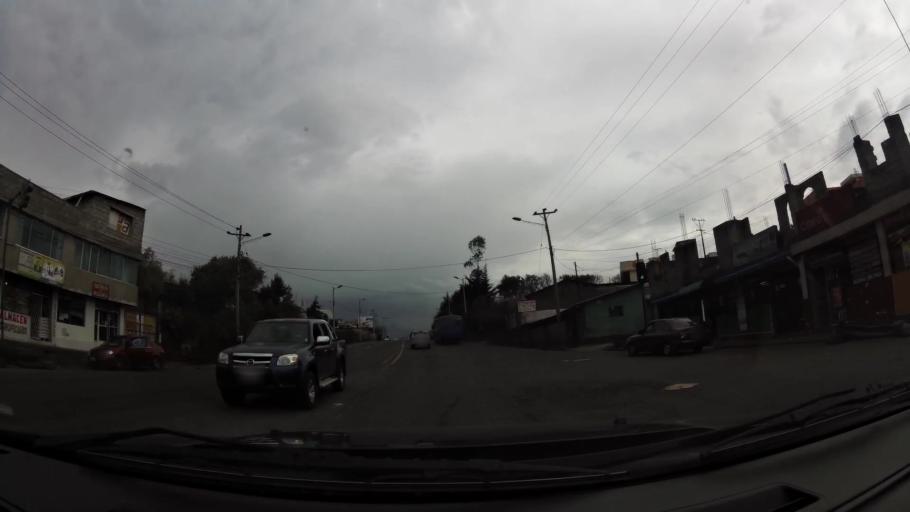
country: EC
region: Pichincha
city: Sangolqui
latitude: -0.3662
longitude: -78.5509
